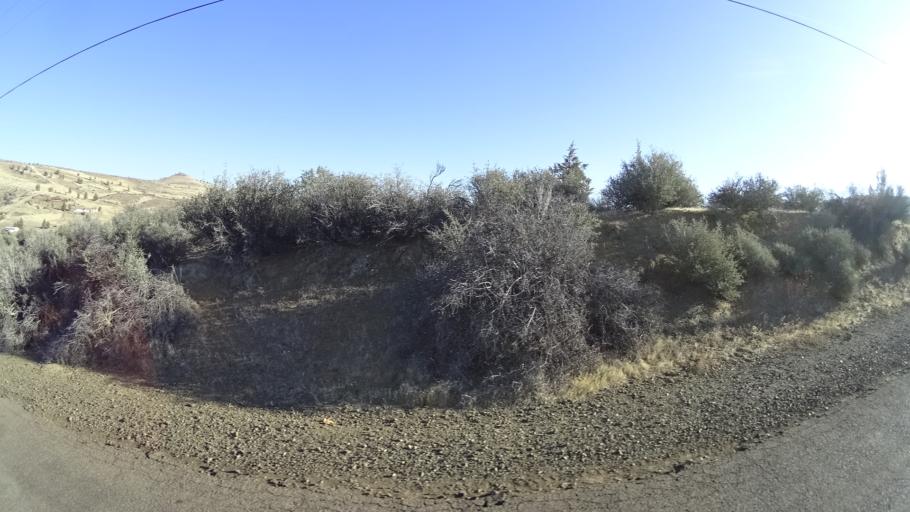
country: US
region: California
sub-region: Siskiyou County
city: Montague
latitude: 41.8947
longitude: -122.4868
